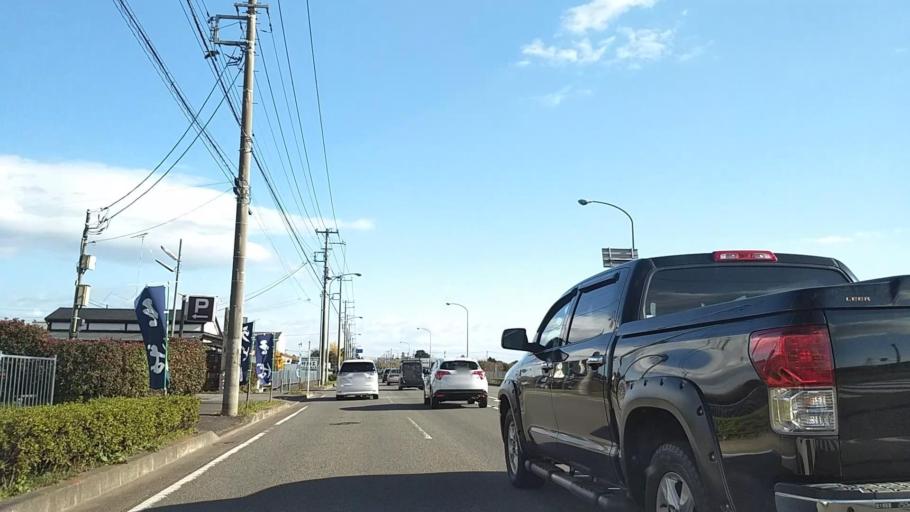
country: JP
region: Tokyo
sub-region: Machida-shi
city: Machida
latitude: 35.5630
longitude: 139.5168
